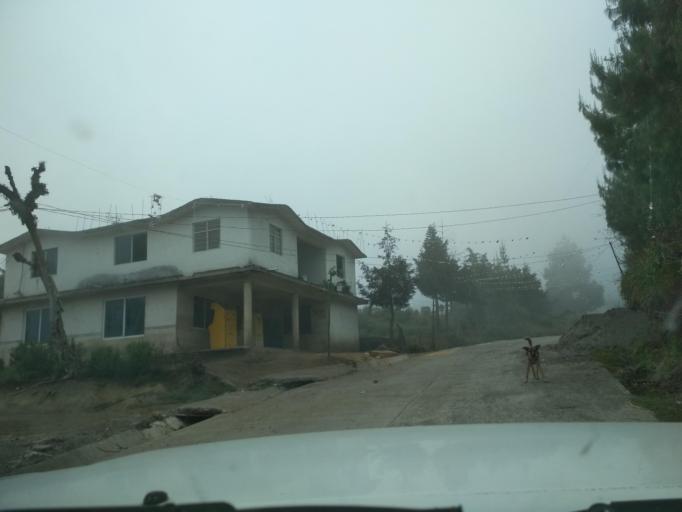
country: MX
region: Veracruz
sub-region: La Perla
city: Chilapa
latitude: 18.9828
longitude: -97.1971
